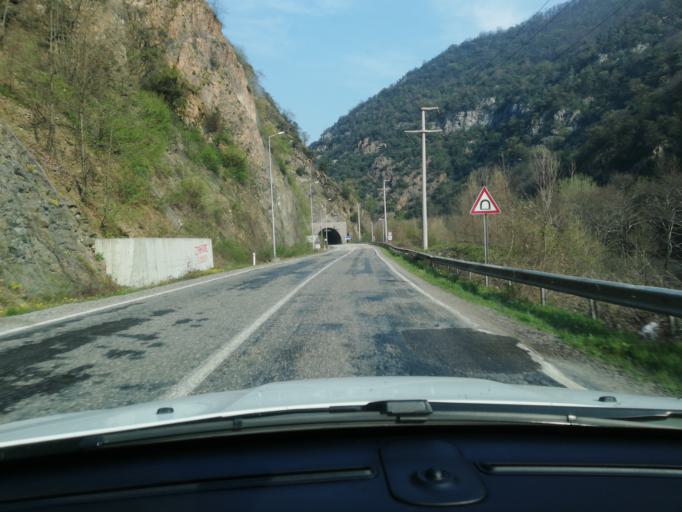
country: TR
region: Karabuk
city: Yenice
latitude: 41.1596
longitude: 32.4596
